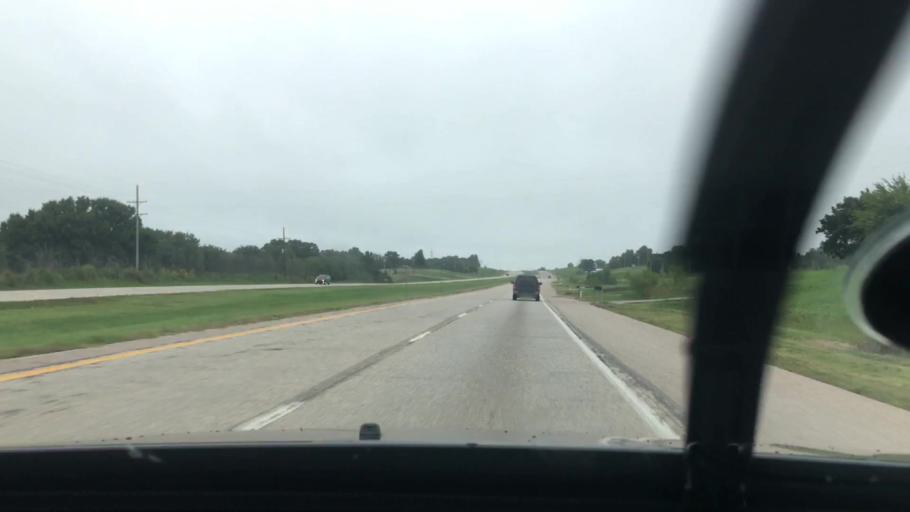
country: US
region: Oklahoma
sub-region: Seminole County
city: Seminole
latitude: 35.2976
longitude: -96.6708
